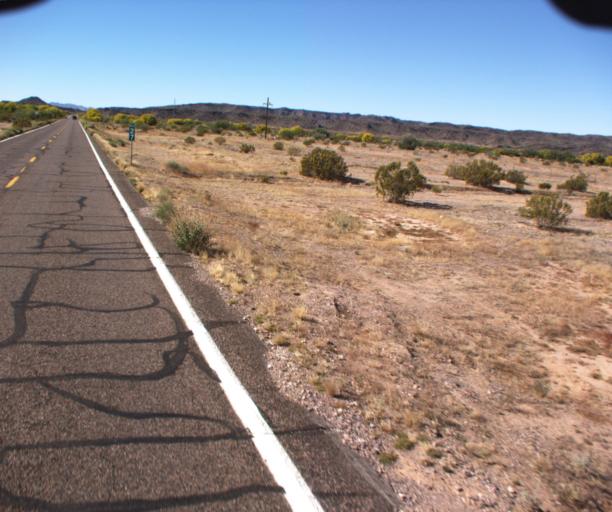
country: US
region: Arizona
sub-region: Pima County
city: Ajo
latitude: 32.5854
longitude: -112.8730
